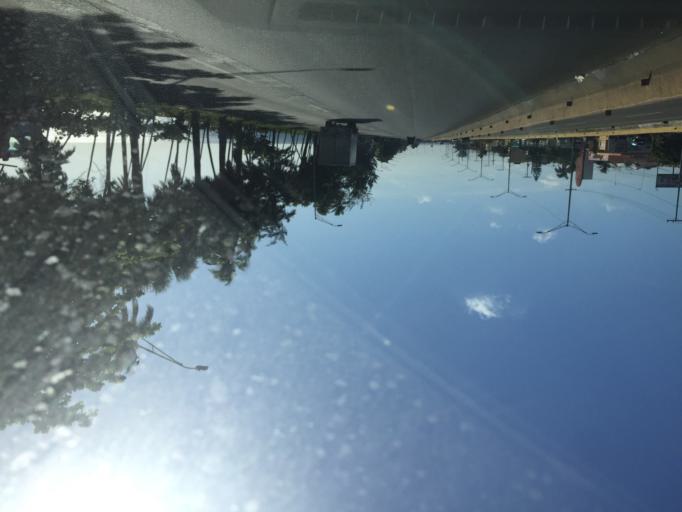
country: DO
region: Santo Domingo
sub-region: Santo Domingo
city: Santo Domingo Este
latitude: 18.4665
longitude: -69.8244
